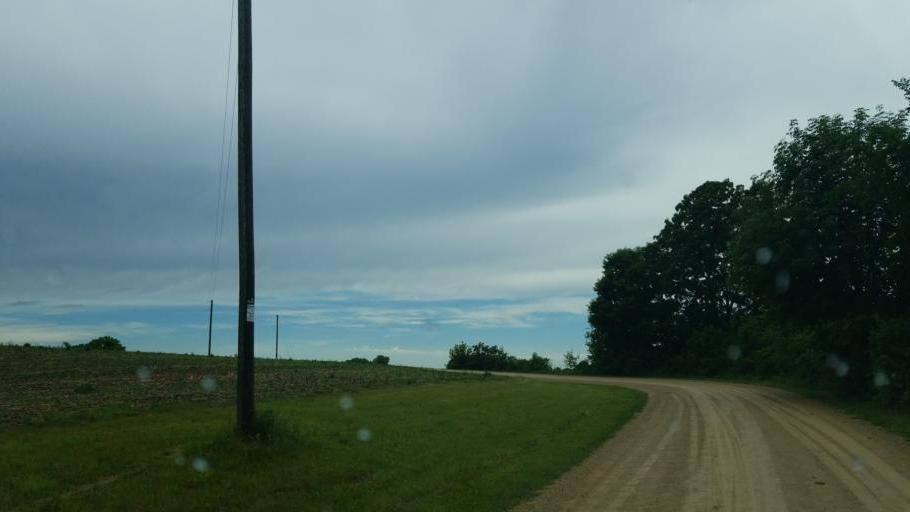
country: US
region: Wisconsin
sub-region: Vernon County
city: Hillsboro
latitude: 43.5888
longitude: -90.3812
